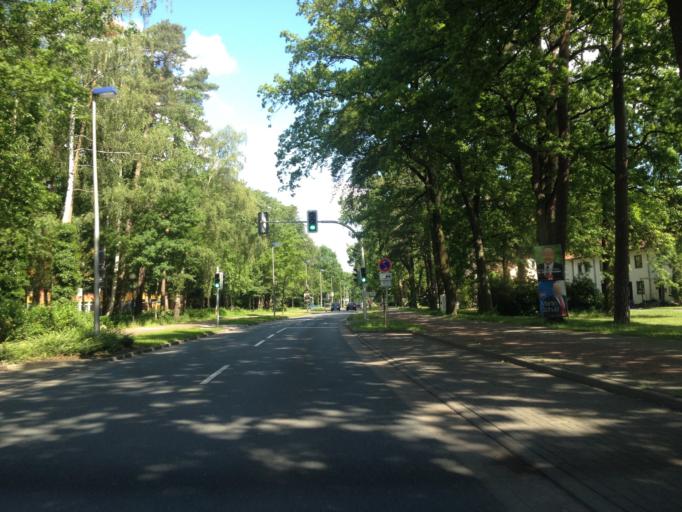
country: DE
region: North Rhine-Westphalia
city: Espelkamp
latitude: 52.3818
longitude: 8.6305
